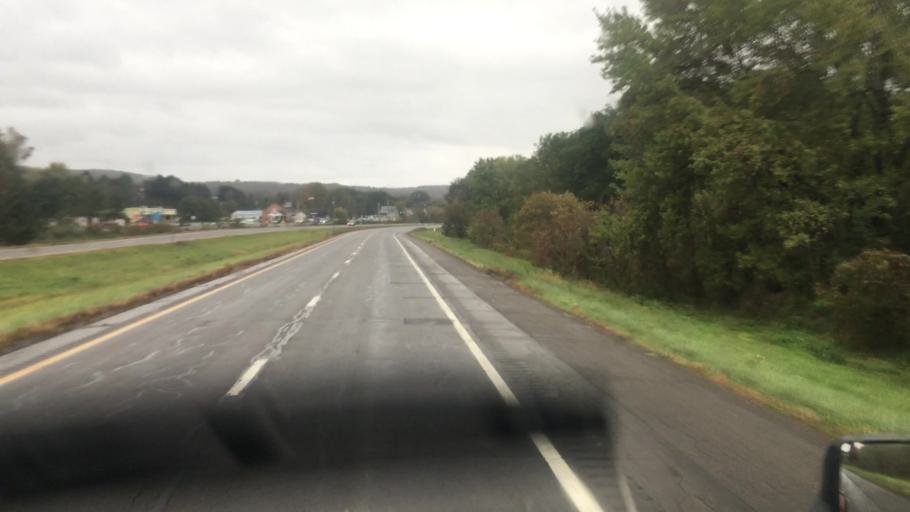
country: US
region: New York
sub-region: Tioga County
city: Apalachin
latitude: 42.0643
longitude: -76.1180
